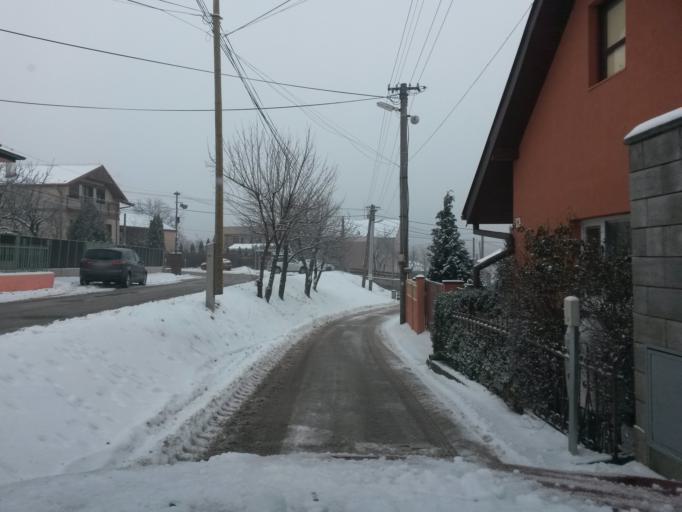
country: SK
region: Kosicky
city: Kosice
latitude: 48.7274
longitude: 21.3023
